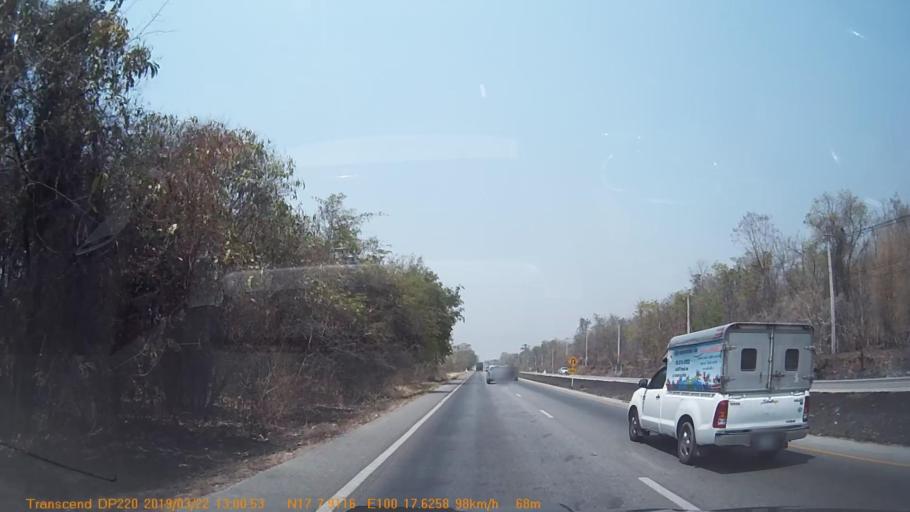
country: TH
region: Phitsanulok
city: Phrom Phiram
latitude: 17.1323
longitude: 100.2936
